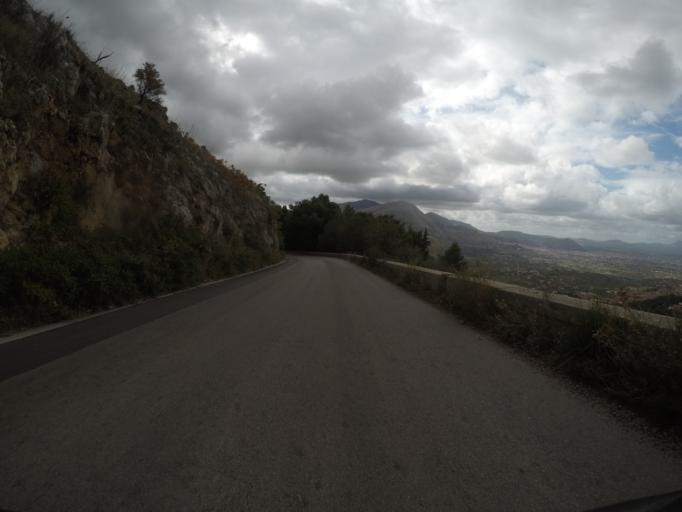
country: IT
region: Sicily
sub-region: Palermo
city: Montelepre
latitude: 38.0960
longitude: 13.1672
